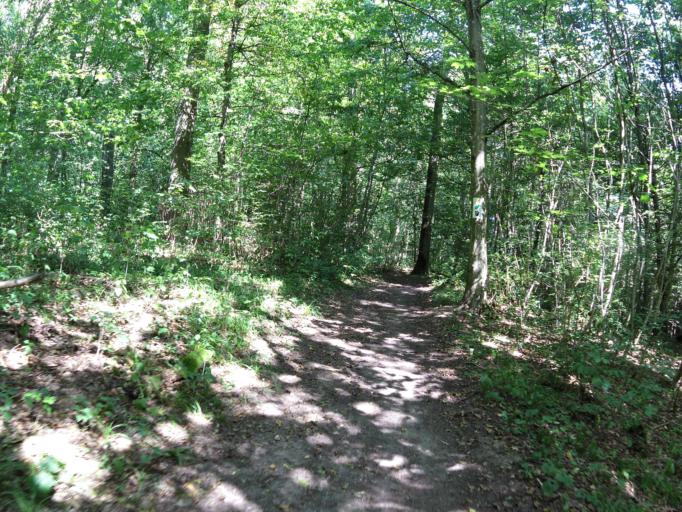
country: DE
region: Bavaria
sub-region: Regierungsbezirk Unterfranken
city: Gadheim
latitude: 49.8458
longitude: 9.8948
